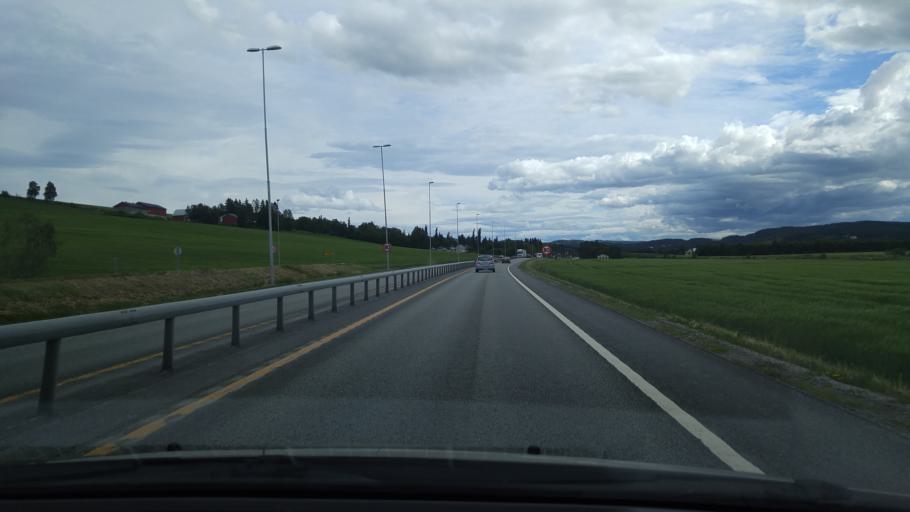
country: NO
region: Nord-Trondelag
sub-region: Steinkjer
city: Steinkjer
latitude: 63.9457
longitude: 11.4184
